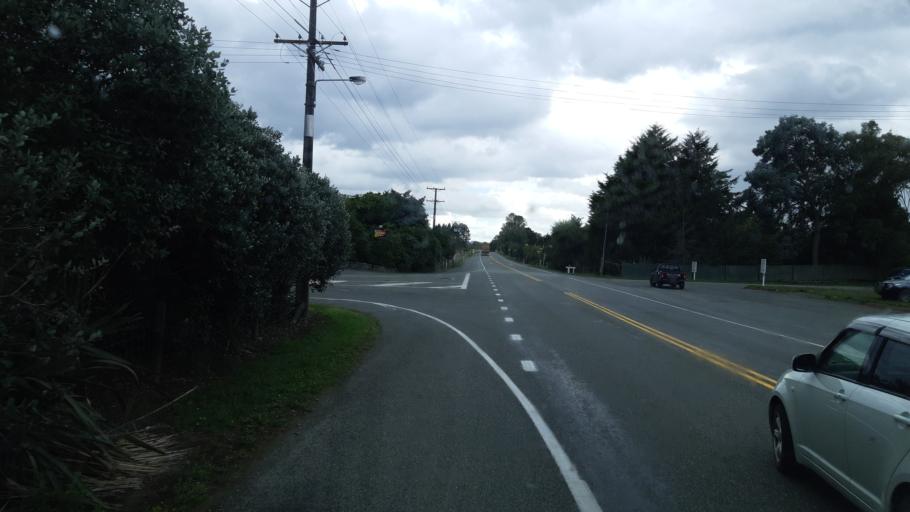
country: NZ
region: Tasman
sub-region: Tasman District
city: Wakefield
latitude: -41.4498
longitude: 172.9589
